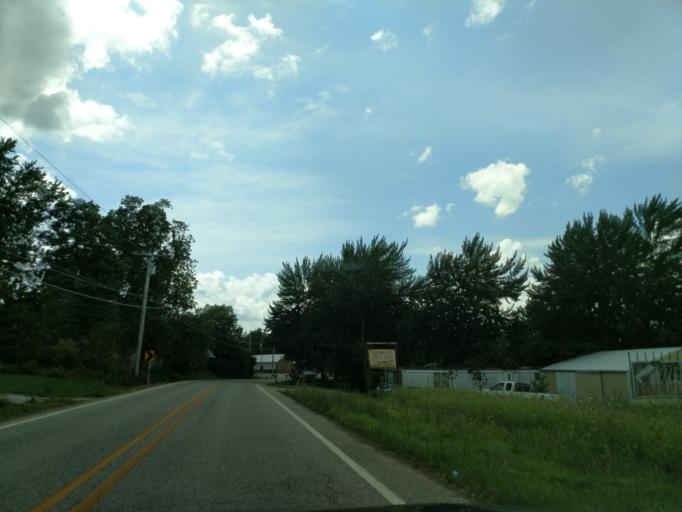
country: US
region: Arkansas
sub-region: Boone County
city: Harrison
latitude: 36.2518
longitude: -93.2187
